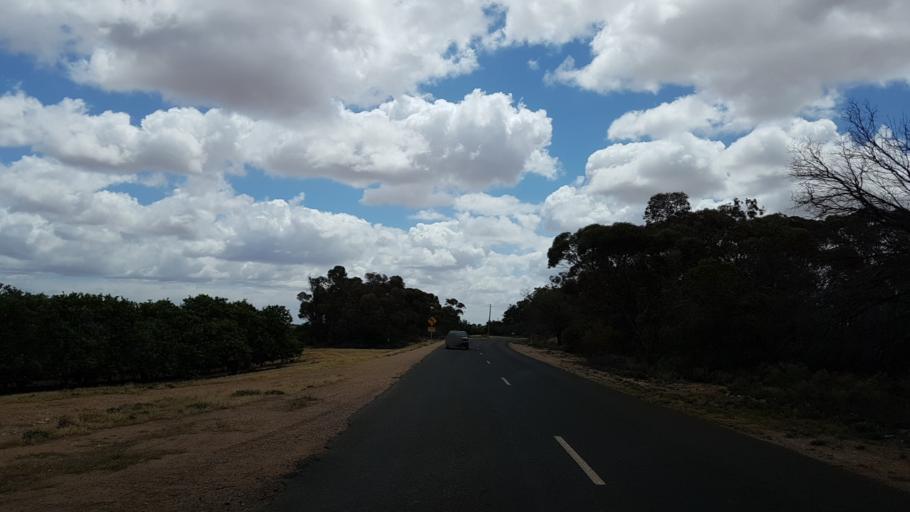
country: AU
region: South Australia
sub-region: Loxton Waikerie
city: Waikerie
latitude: -34.1796
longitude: 140.0253
